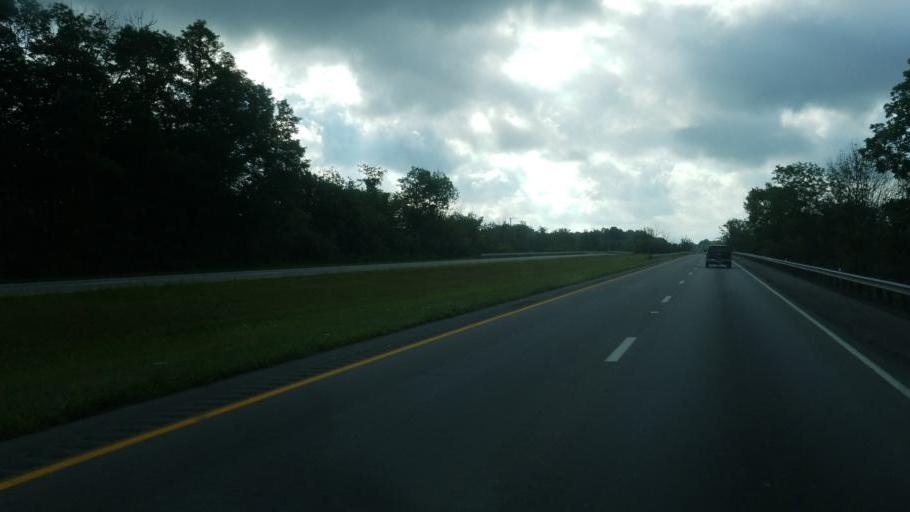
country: US
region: Ohio
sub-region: Stark County
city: Brewster
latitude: 40.7803
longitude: -81.6060
